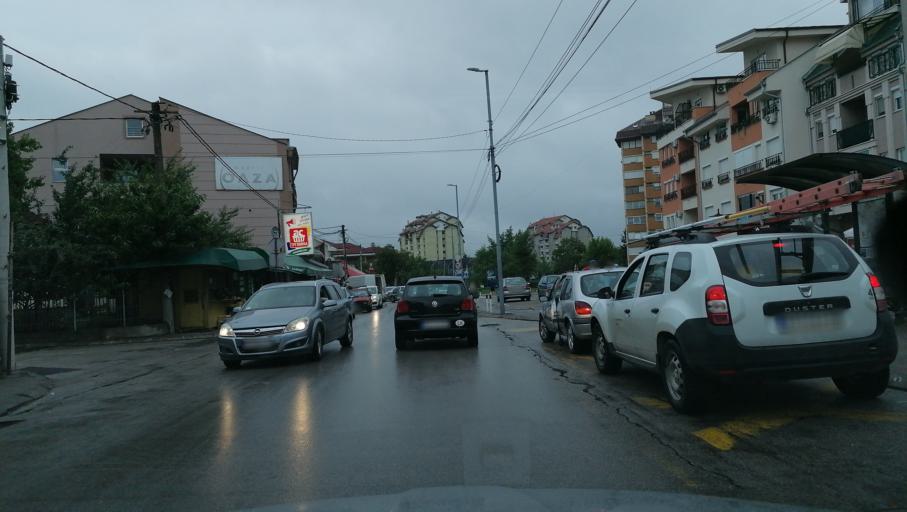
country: RS
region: Central Serbia
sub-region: Rasinski Okrug
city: Krusevac
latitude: 43.5701
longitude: 21.3298
